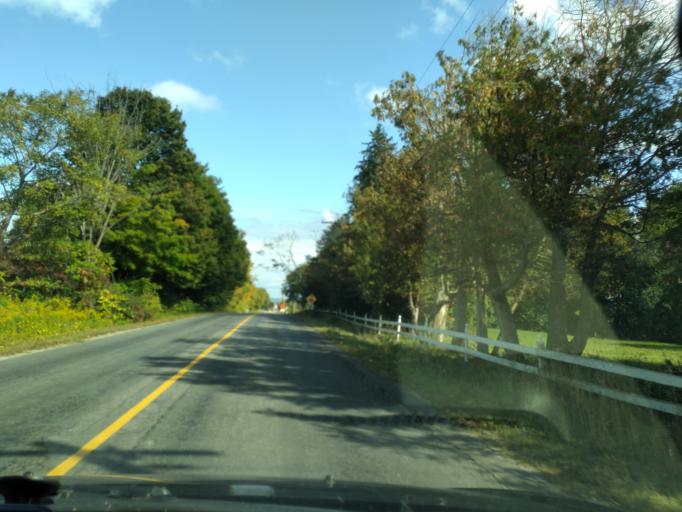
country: CA
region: Ontario
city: Innisfil
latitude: 44.2835
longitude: -79.5755
